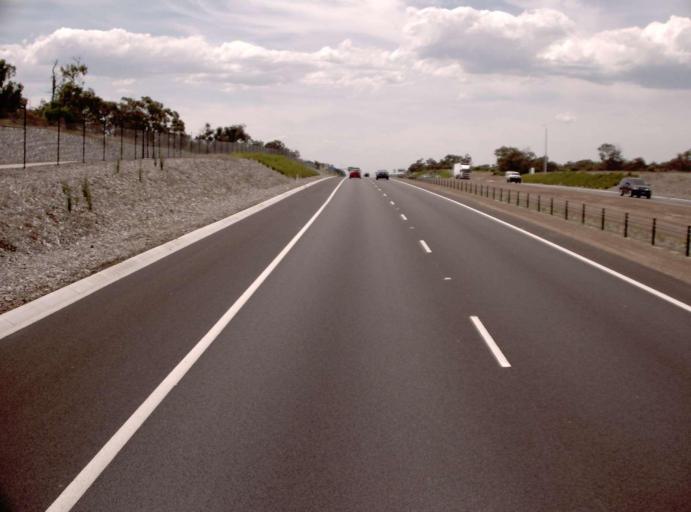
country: AU
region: Victoria
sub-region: Frankston
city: Langwarrin
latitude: -38.1736
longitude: 145.1625
